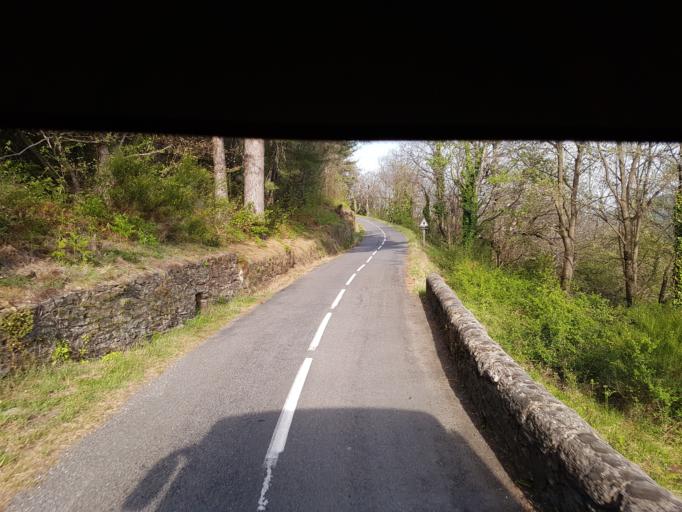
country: FR
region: Languedoc-Roussillon
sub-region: Departement du Gard
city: Branoux-les-Taillades
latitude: 44.3300
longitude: 3.9182
